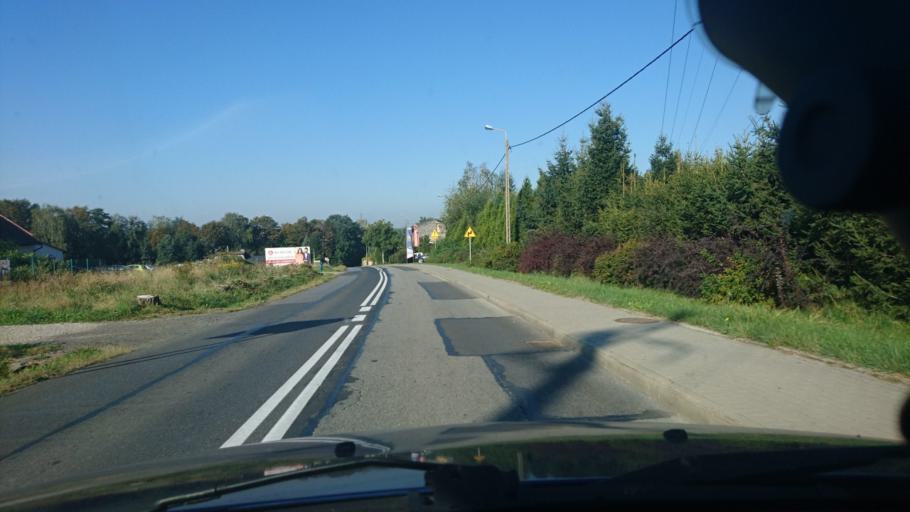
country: PL
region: Silesian Voivodeship
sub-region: Bielsko-Biala
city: Bielsko-Biala
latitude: 49.8507
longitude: 19.0721
